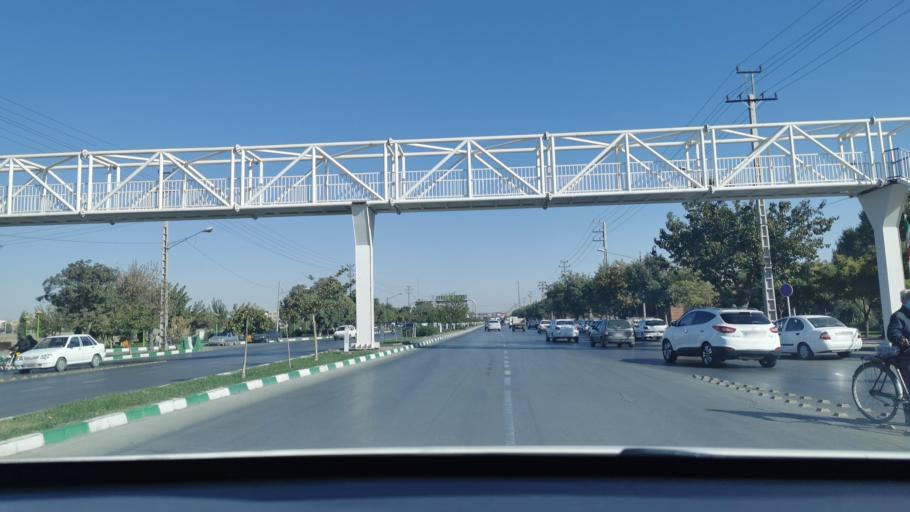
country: IR
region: Razavi Khorasan
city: Mashhad
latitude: 36.3312
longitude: 59.6249
